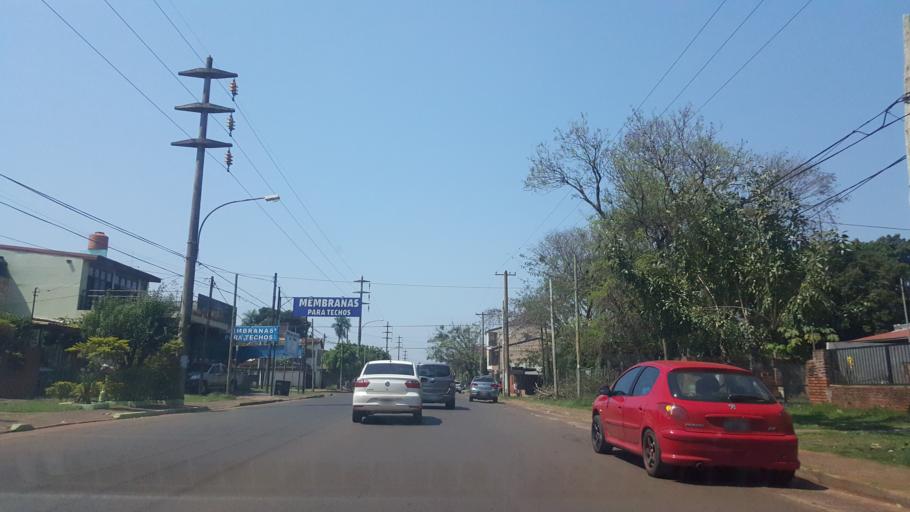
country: AR
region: Misiones
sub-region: Departamento de Capital
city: Posadas
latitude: -27.3761
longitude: -55.9128
